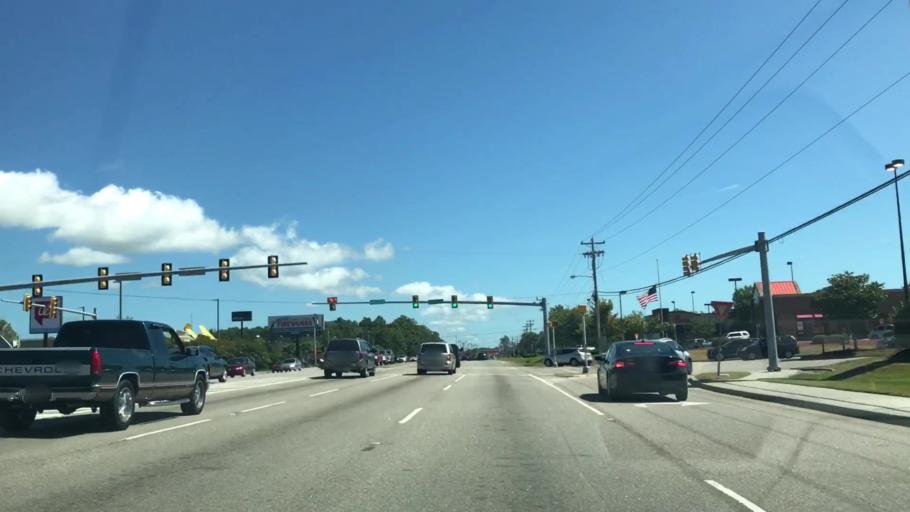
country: US
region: South Carolina
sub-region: Horry County
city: North Myrtle Beach
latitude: 33.8328
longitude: -78.6741
